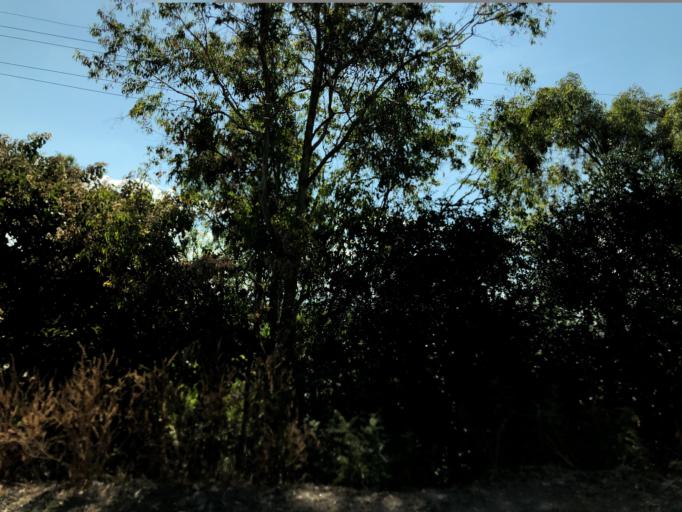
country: ET
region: Amhara
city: Lalibela
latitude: 12.0300
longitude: 39.0435
